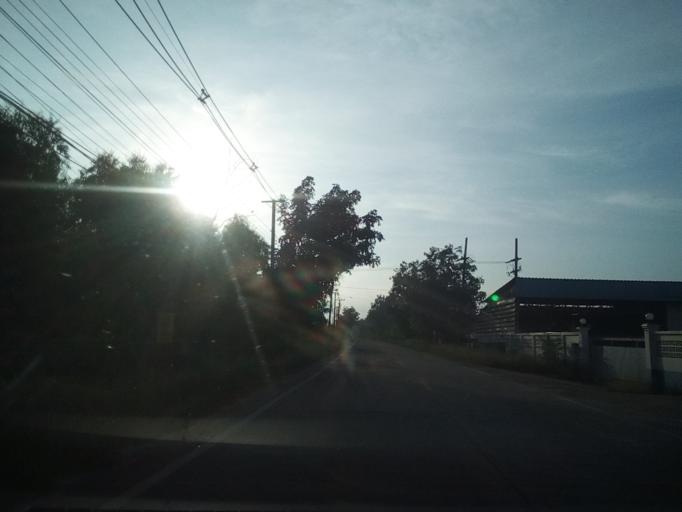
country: TH
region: Lamphun
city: Ban Thi
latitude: 18.6246
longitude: 99.0747
